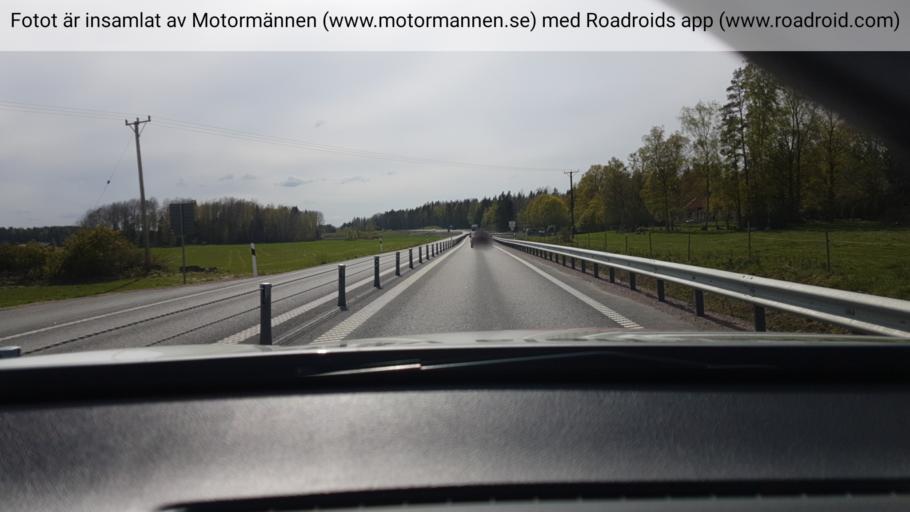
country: SE
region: Uppsala
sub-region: Osthammars Kommun
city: Gimo
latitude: 60.1476
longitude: 18.1698
